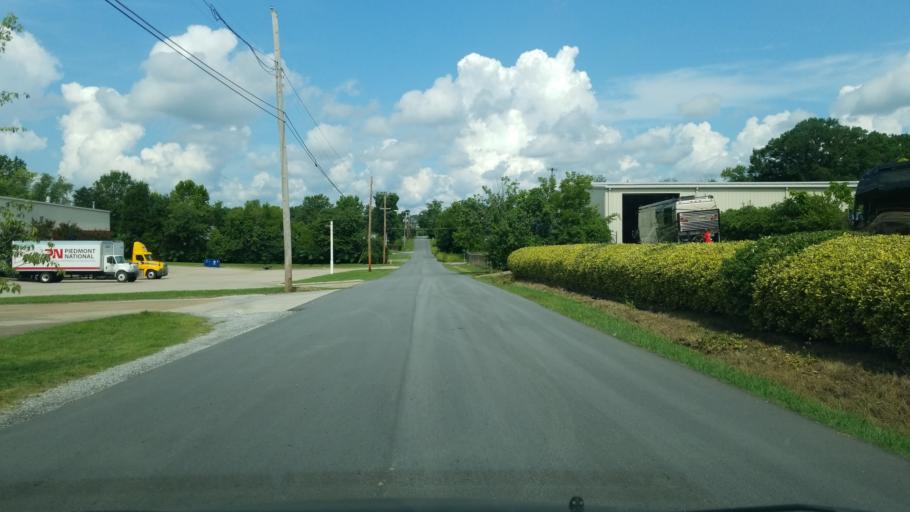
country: US
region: Tennessee
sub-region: Hamilton County
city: East Chattanooga
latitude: 35.0708
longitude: -85.2619
